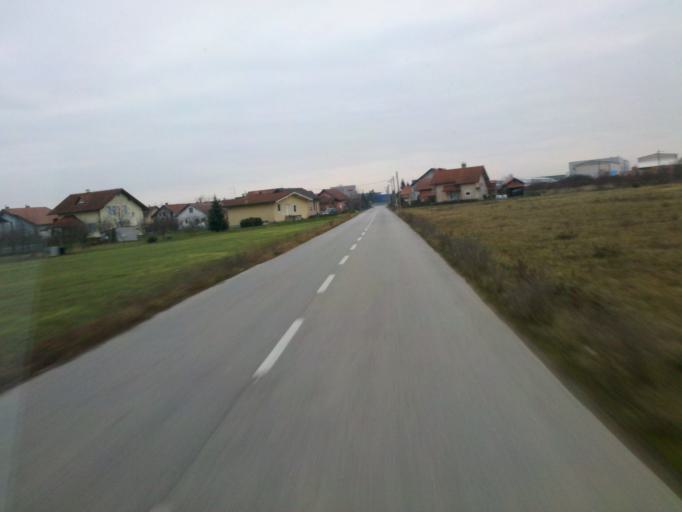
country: HR
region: Grad Zagreb
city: Lucko
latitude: 45.7573
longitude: 15.8745
